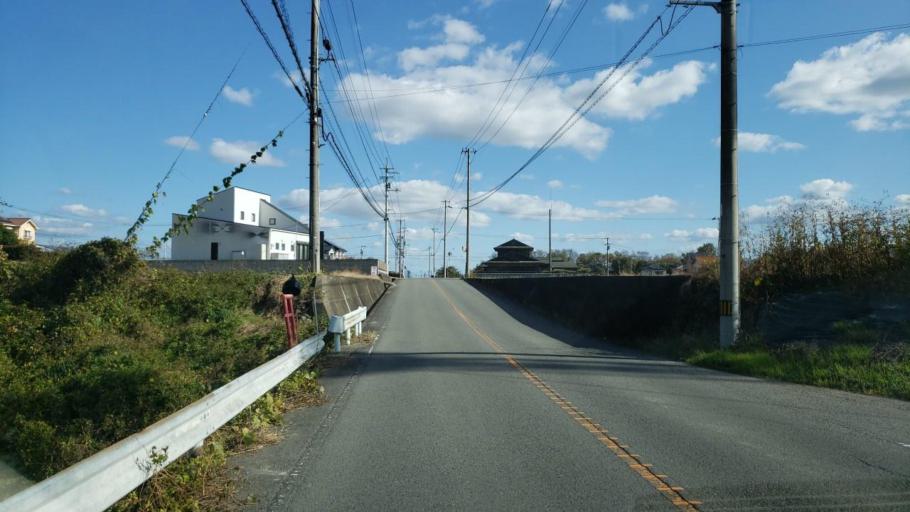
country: JP
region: Tokushima
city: Wakimachi
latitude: 34.0819
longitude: 134.2168
